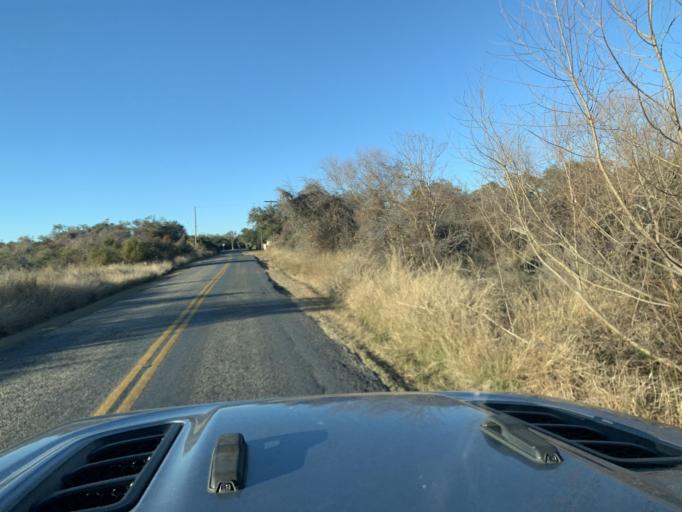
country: US
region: Texas
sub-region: Aransas County
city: Fulton
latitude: 28.1366
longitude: -96.9843
